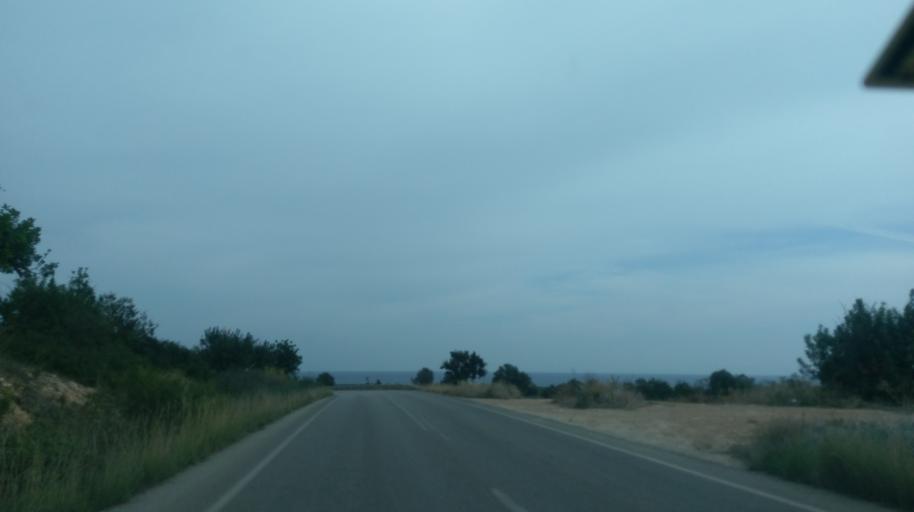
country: CY
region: Ammochostos
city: Leonarisso
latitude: 35.4017
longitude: 34.1020
